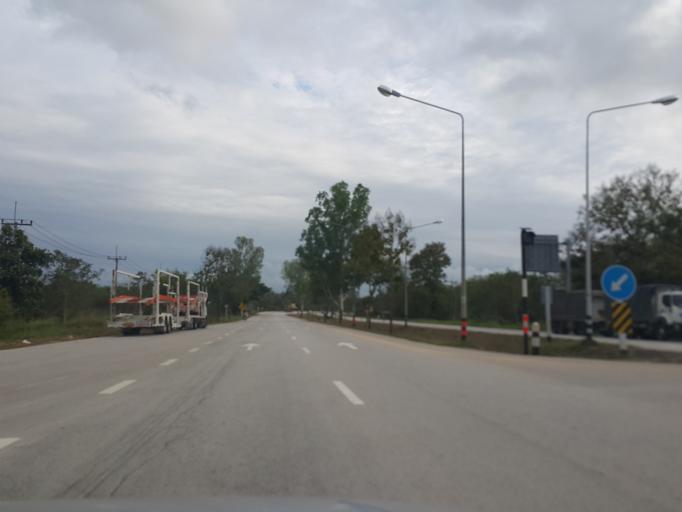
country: TH
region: Lampang
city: Ko Kha
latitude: 18.1843
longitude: 99.4084
